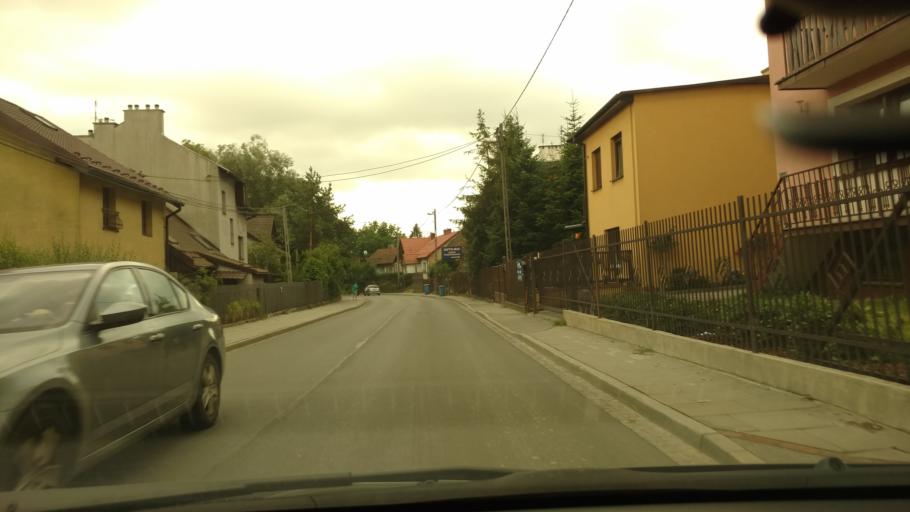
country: PL
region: Lesser Poland Voivodeship
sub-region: Powiat krakowski
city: Zielonki
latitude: 50.1066
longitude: 19.9431
